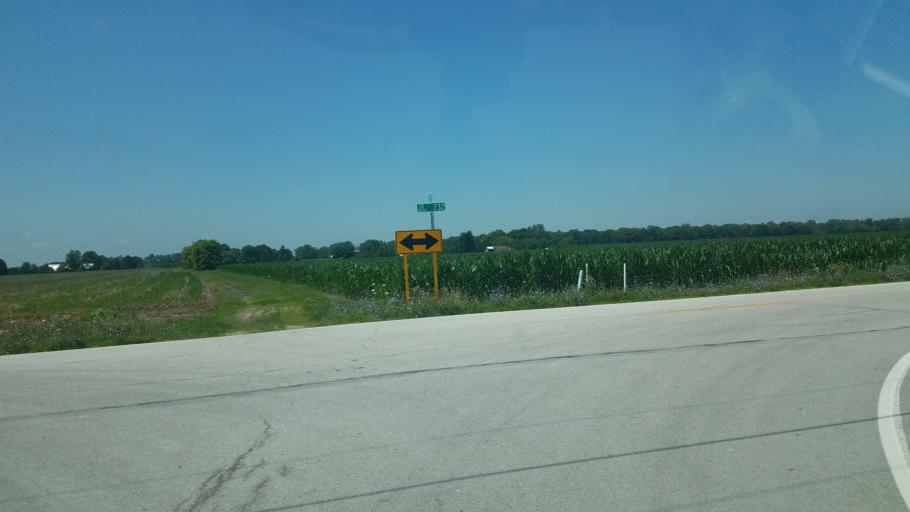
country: US
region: Ohio
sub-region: Sandusky County
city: Clyde
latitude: 41.3924
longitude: -83.0117
